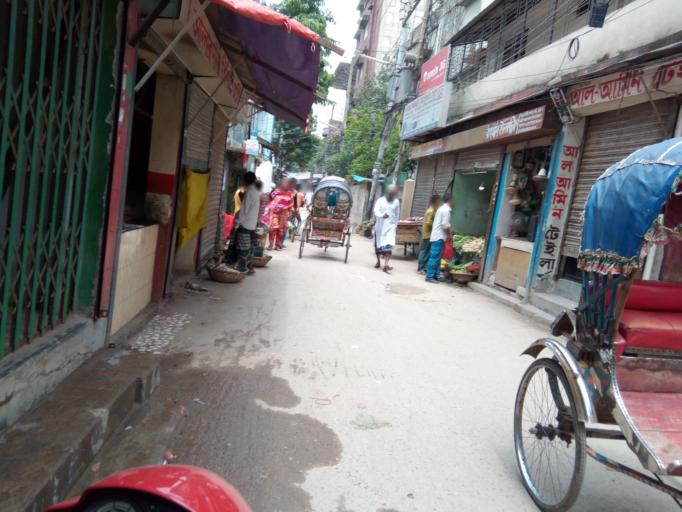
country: BD
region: Dhaka
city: Paltan
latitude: 23.7602
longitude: 90.4246
